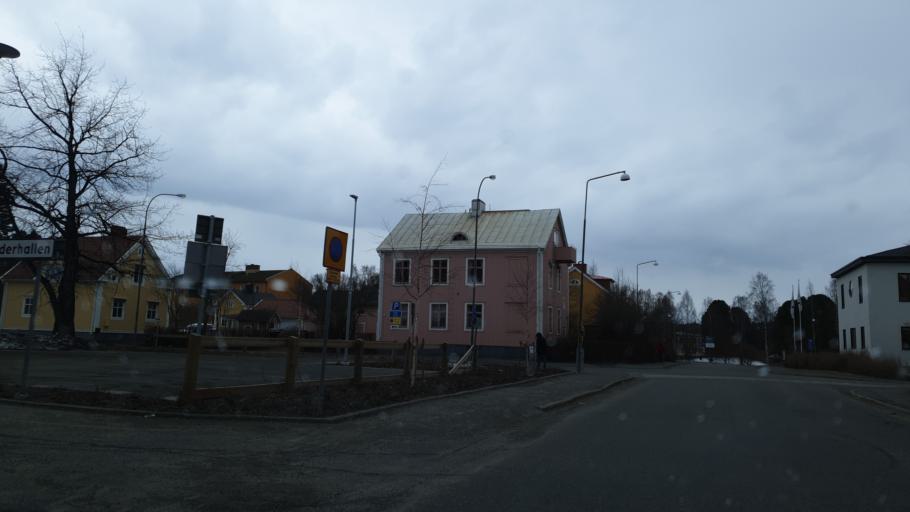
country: SE
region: Vaesterbotten
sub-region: Skelleftea Kommun
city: Skelleftea
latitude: 64.7519
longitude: 20.9401
